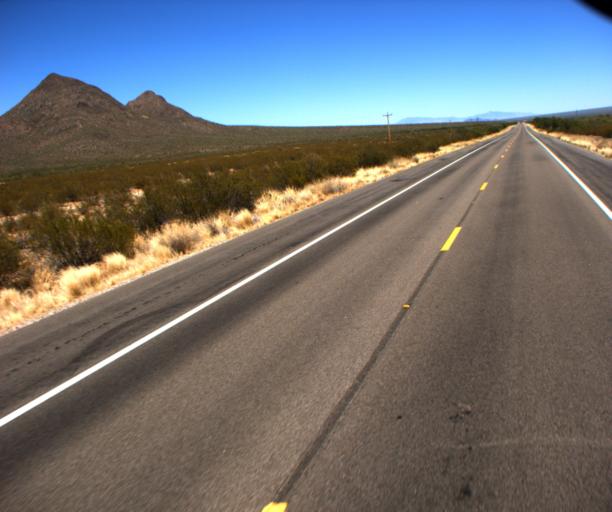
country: US
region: Arizona
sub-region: Pima County
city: Three Points
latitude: 32.0405
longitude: -111.4689
